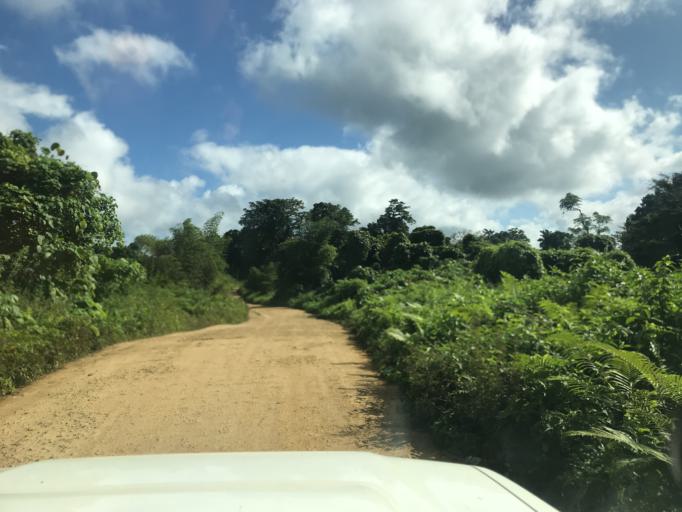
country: VU
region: Sanma
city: Luganville
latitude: -15.5051
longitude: 167.0969
